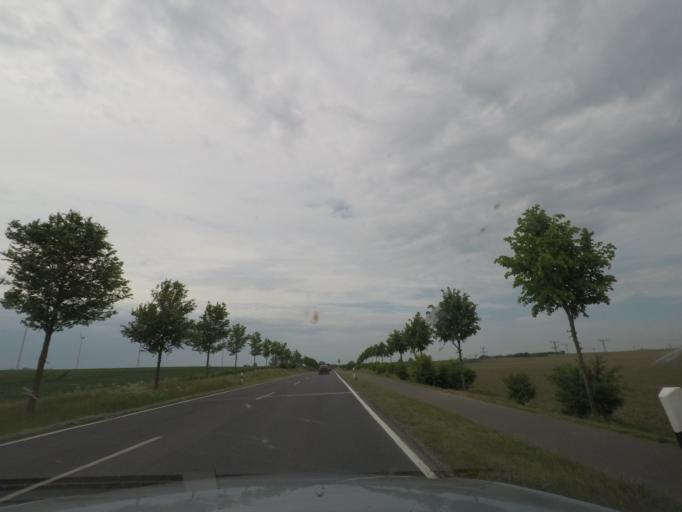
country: DE
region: Brandenburg
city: Schenkenberg
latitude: 53.3426
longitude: 13.9425
